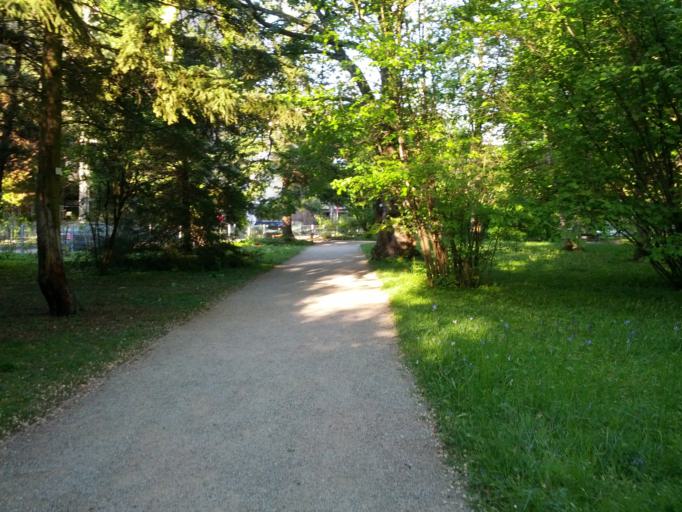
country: DE
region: Baden-Wuerttemberg
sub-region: Karlsruhe Region
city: Heidelberg
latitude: 49.4153
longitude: 8.6678
